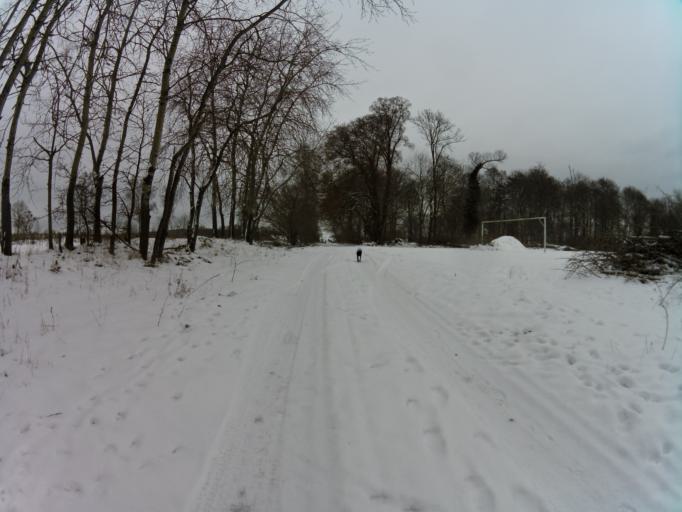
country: PL
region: West Pomeranian Voivodeship
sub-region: Powiat choszczenski
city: Recz
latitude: 53.3411
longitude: 15.5410
